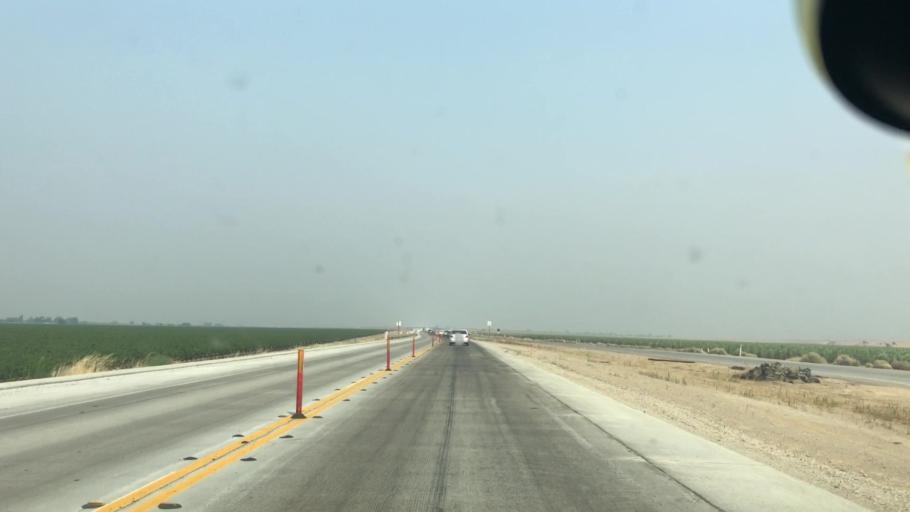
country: US
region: California
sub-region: San Joaquin County
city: Tracy
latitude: 37.6380
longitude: -121.3792
